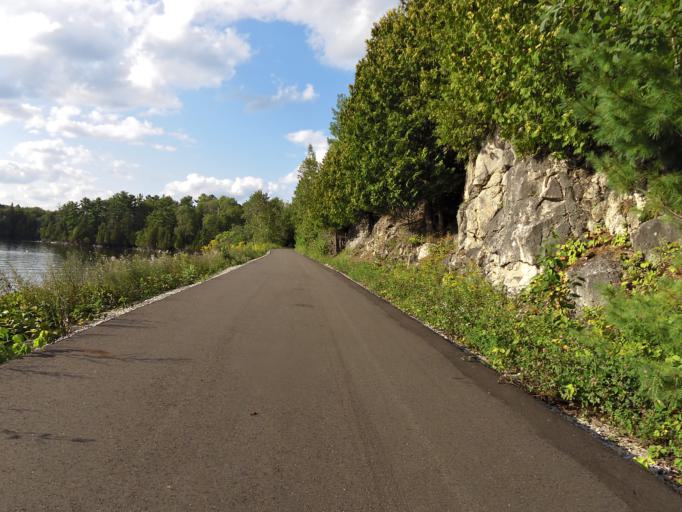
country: CA
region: Quebec
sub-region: Outaouais
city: Maniwaki
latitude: 46.2183
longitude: -76.0439
